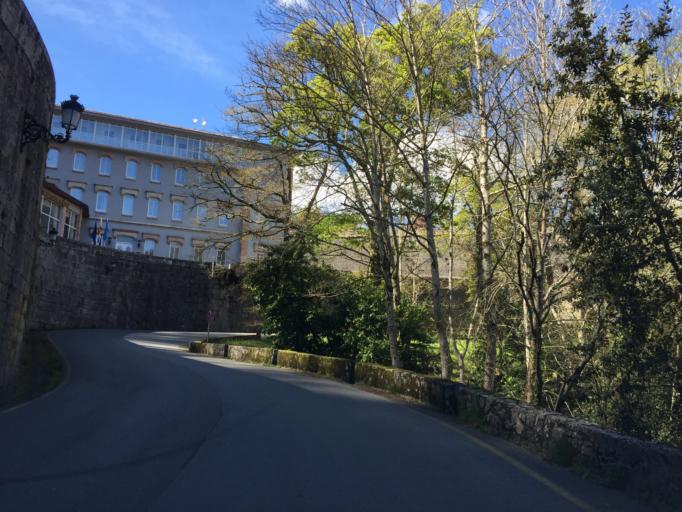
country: ES
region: Asturias
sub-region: Province of Asturias
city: Amieva
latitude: 43.3077
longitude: -5.0539
